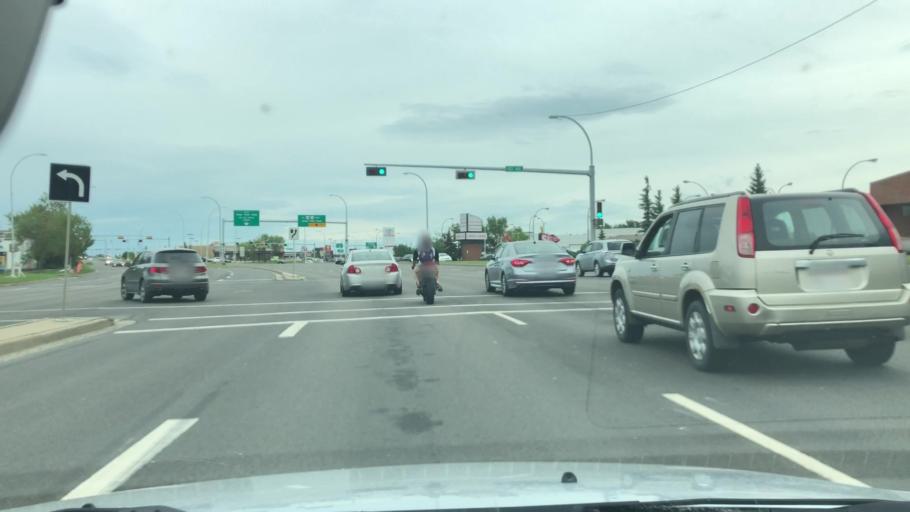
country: CA
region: Alberta
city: St. Albert
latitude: 53.5455
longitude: -113.6160
